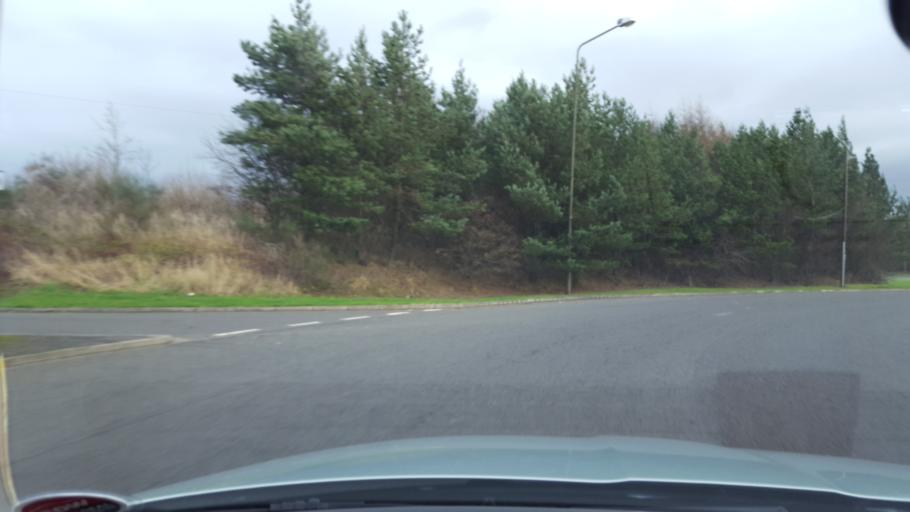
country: GB
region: Scotland
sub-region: West Lothian
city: Mid Calder
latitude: 55.8774
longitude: -3.4870
